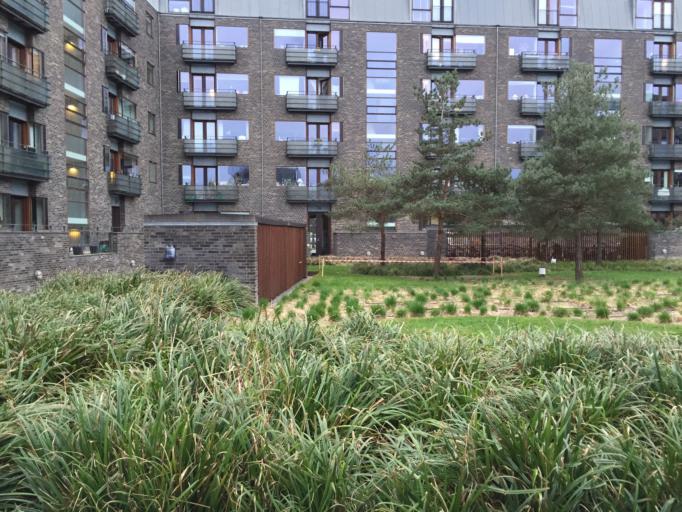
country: DK
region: Capital Region
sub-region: Kobenhavn
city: Christianshavn
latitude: 55.7045
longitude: 12.5883
